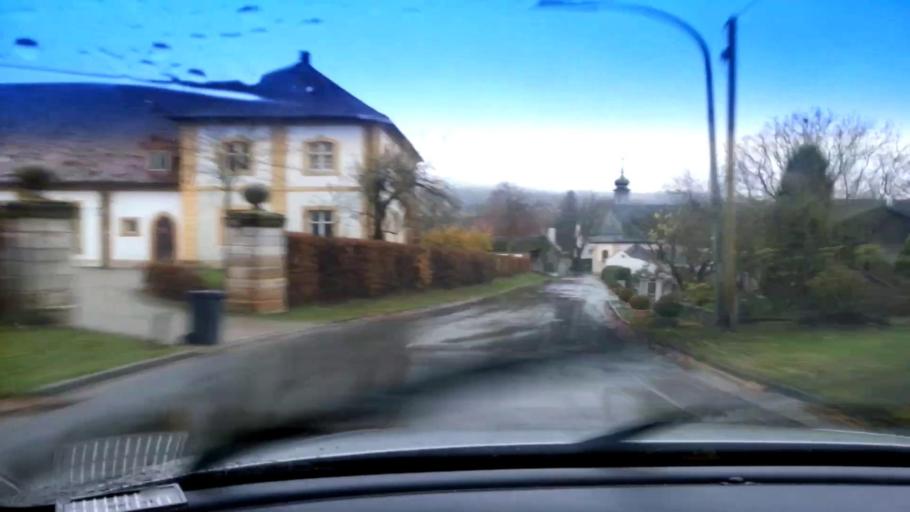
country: DE
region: Bavaria
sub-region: Upper Franconia
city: Schesslitz
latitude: 49.9509
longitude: 11.0360
